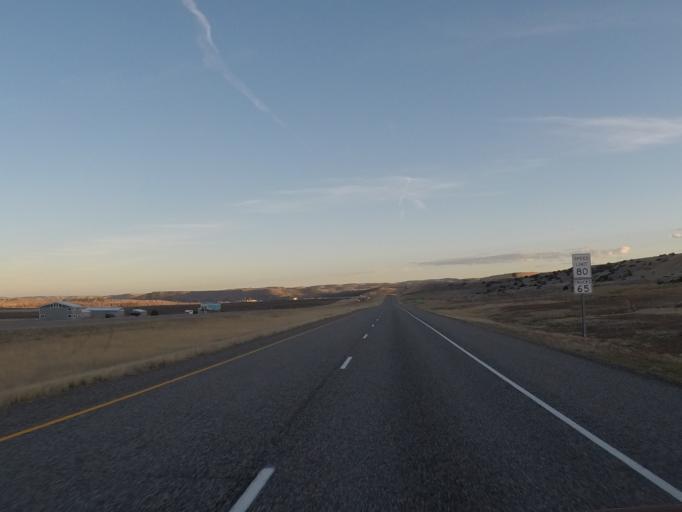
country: US
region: Montana
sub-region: Sweet Grass County
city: Big Timber
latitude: 45.7613
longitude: -109.7869
